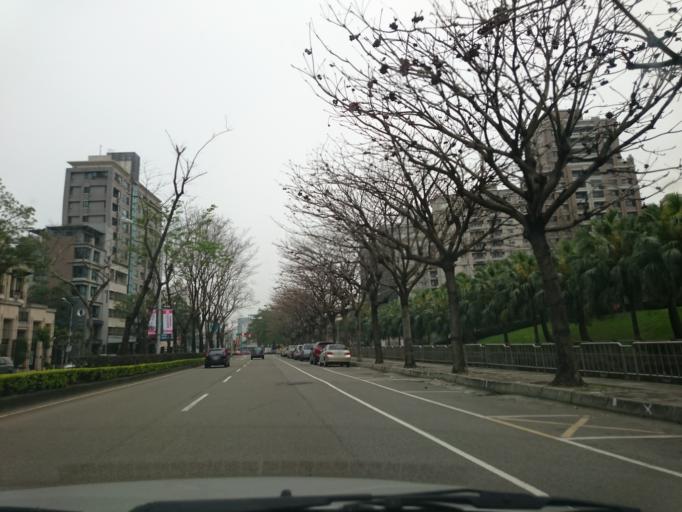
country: TW
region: Taiwan
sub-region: Taichung City
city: Taichung
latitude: 24.1440
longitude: 120.6406
